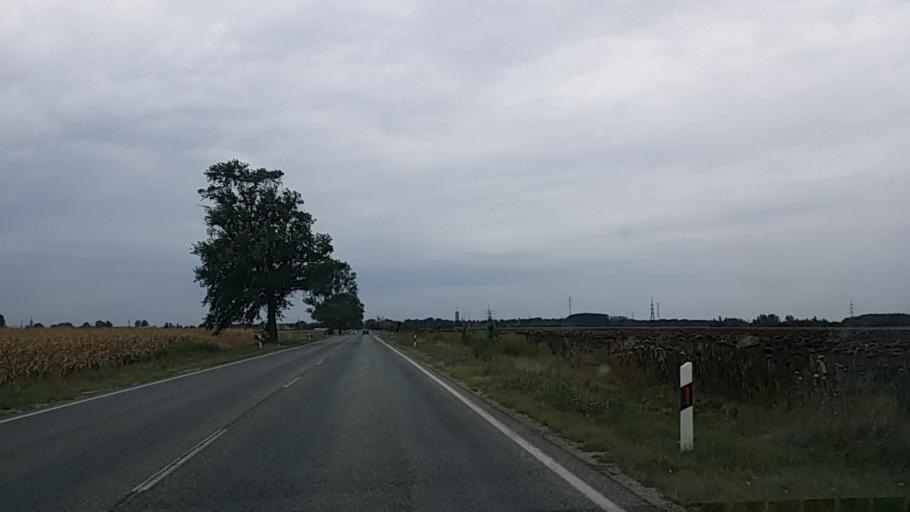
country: HU
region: Gyor-Moson-Sopron
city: Kapuvar
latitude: 47.5899
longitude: 17.0634
